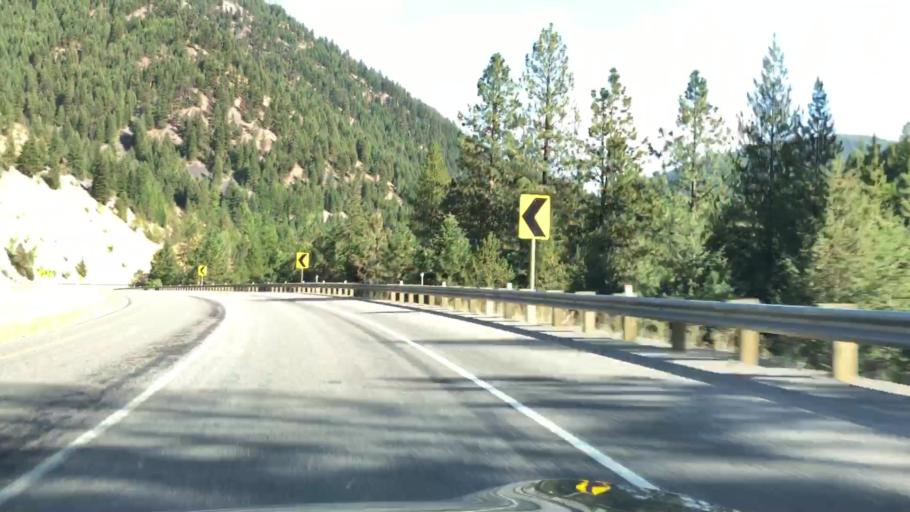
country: US
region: Montana
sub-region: Sanders County
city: Thompson Falls
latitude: 47.3275
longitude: -115.2557
